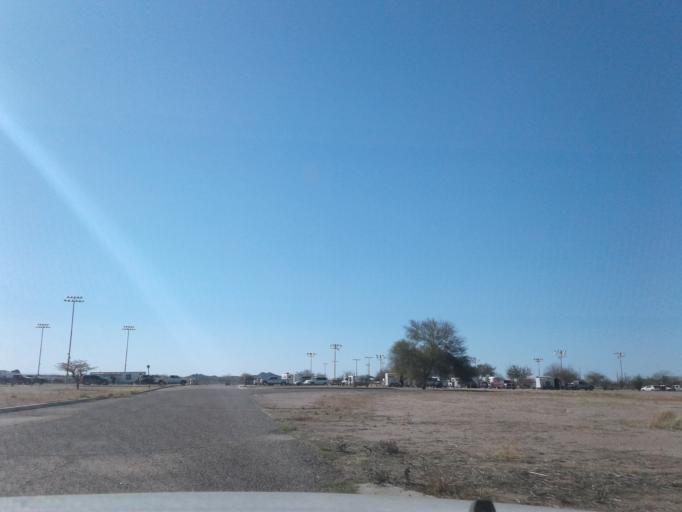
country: US
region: Arizona
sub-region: Maricopa County
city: Paradise Valley
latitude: 33.6624
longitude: -111.9827
